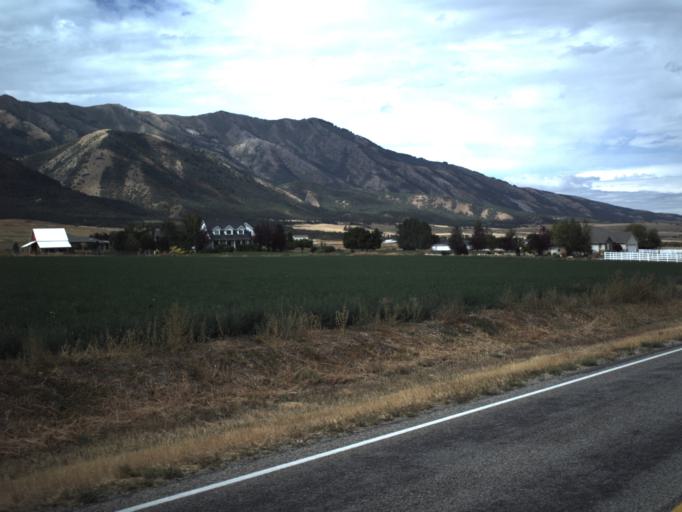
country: US
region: Utah
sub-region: Cache County
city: Wellsville
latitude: 41.6602
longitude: -111.9462
